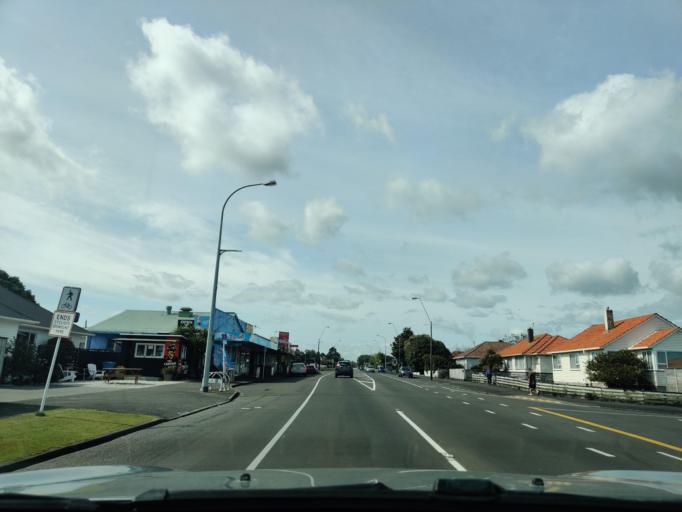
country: NZ
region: Taranaki
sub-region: New Plymouth District
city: New Plymouth
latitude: -39.0692
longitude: 174.0898
